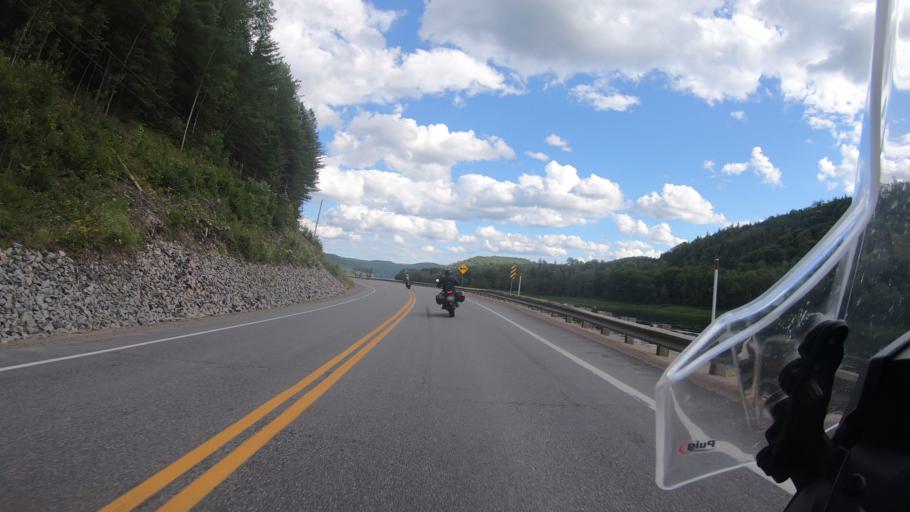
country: CA
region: Quebec
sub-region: Mauricie
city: Saint-Tite
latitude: 46.9989
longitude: -72.9234
